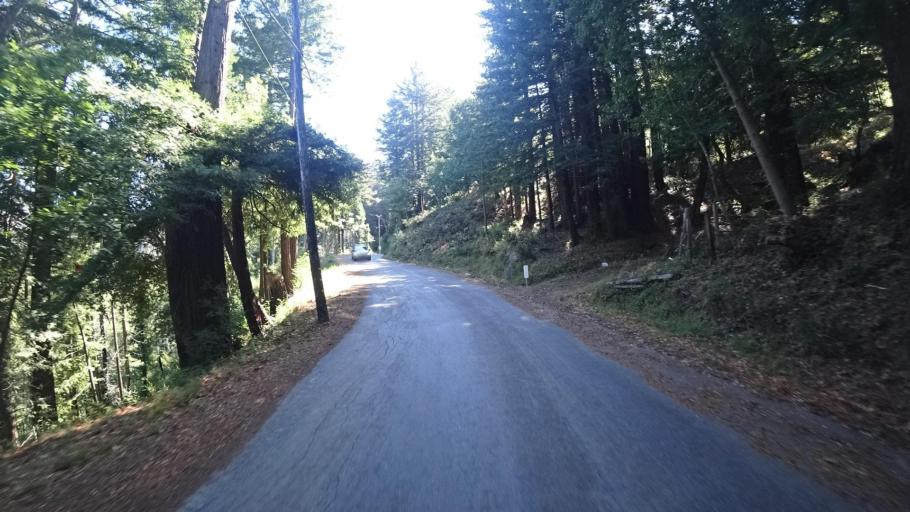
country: US
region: California
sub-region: Monterey County
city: Carmel Valley Village
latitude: 36.3777
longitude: -121.8586
